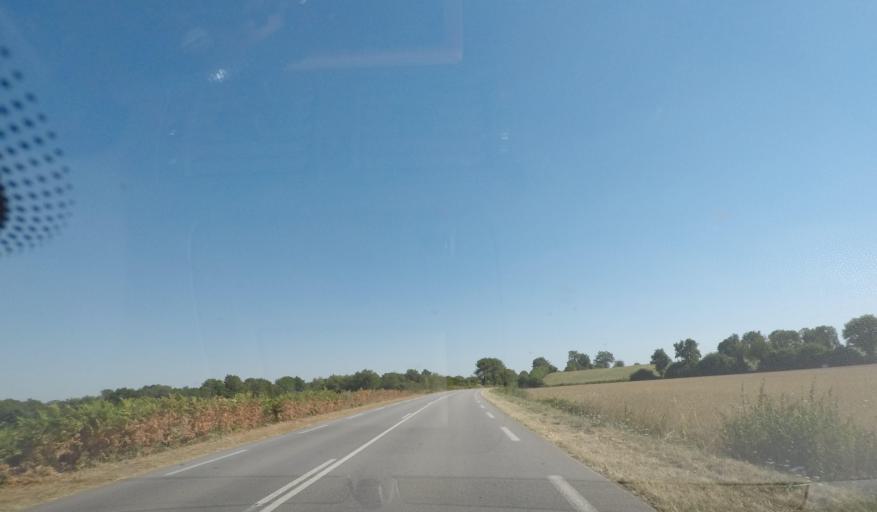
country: FR
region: Brittany
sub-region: Departement du Morbihan
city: Peaule
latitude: 47.6055
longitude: -2.3846
